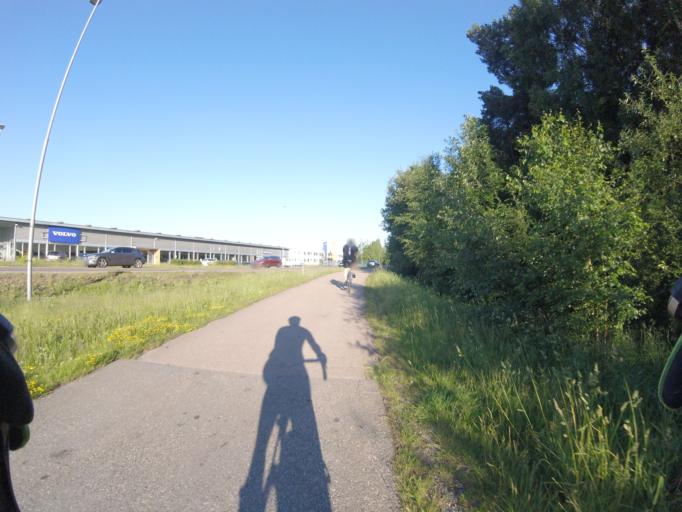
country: NO
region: Akershus
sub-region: Skedsmo
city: Lillestrom
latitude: 59.9627
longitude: 11.0597
